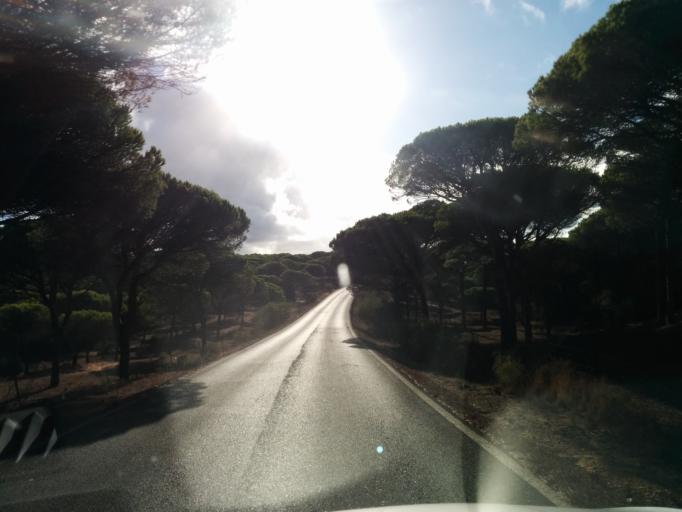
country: ES
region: Andalusia
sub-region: Provincia de Cadiz
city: Vejer de la Frontera
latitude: 36.1927
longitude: -5.9952
